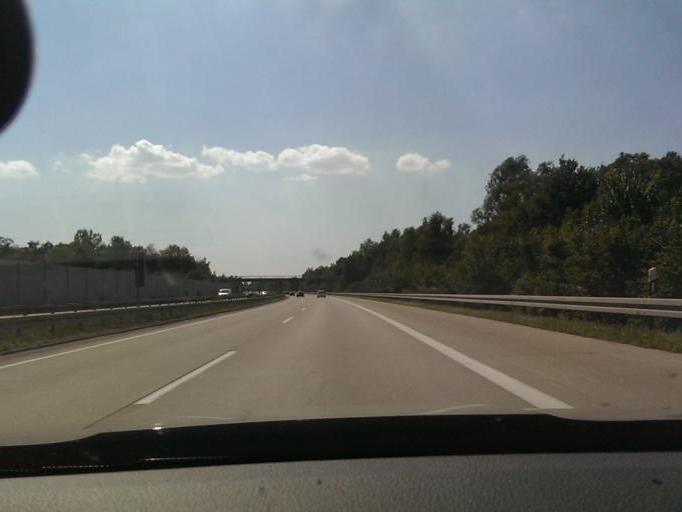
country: DE
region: Lower Saxony
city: Langenhagen
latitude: 52.4852
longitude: 9.7227
